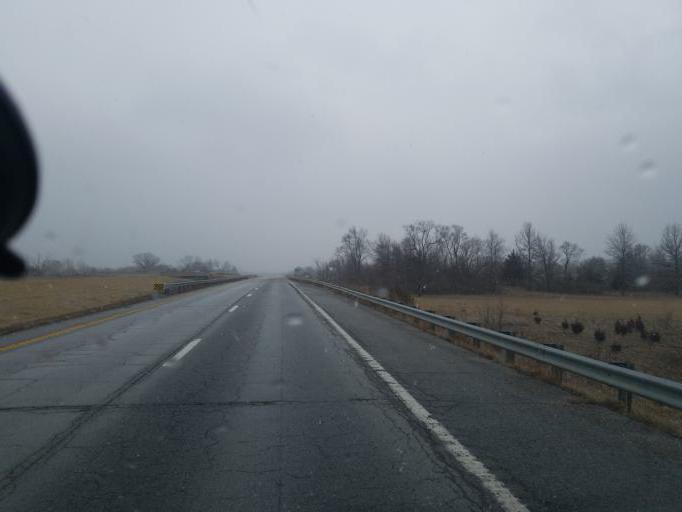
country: US
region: Missouri
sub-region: Macon County
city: La Plata
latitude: 40.0320
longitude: -92.4867
